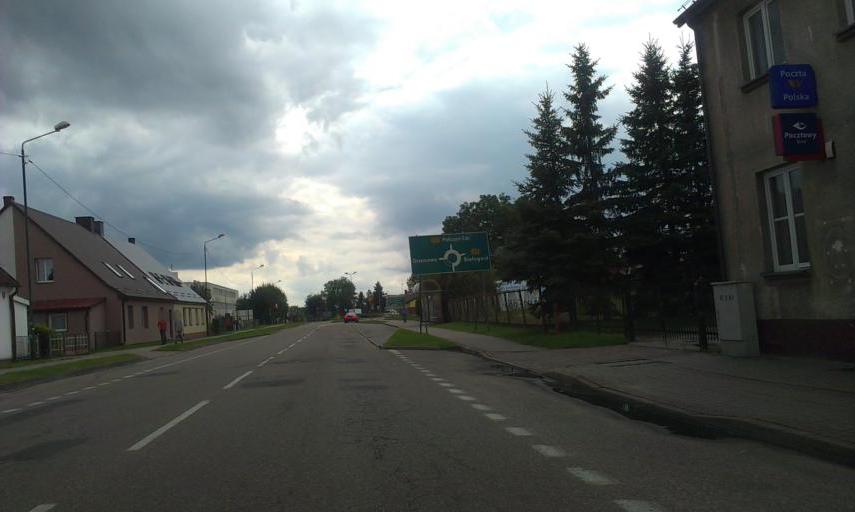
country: PL
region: West Pomeranian Voivodeship
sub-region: Powiat bialogardzki
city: Tychowo
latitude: 53.9265
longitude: 16.2546
